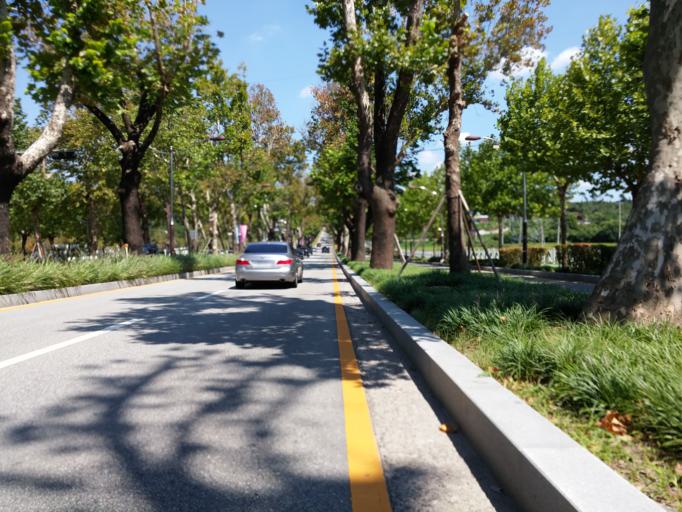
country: KR
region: Chungcheongbuk-do
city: Cheongju-si
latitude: 36.6214
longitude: 127.4040
